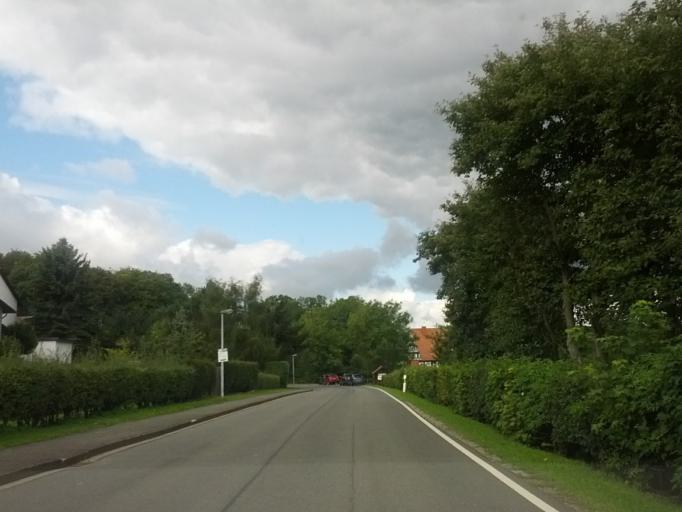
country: DE
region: Hesse
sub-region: Regierungsbezirk Kassel
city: Herleshausen
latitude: 51.0500
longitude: 10.1206
